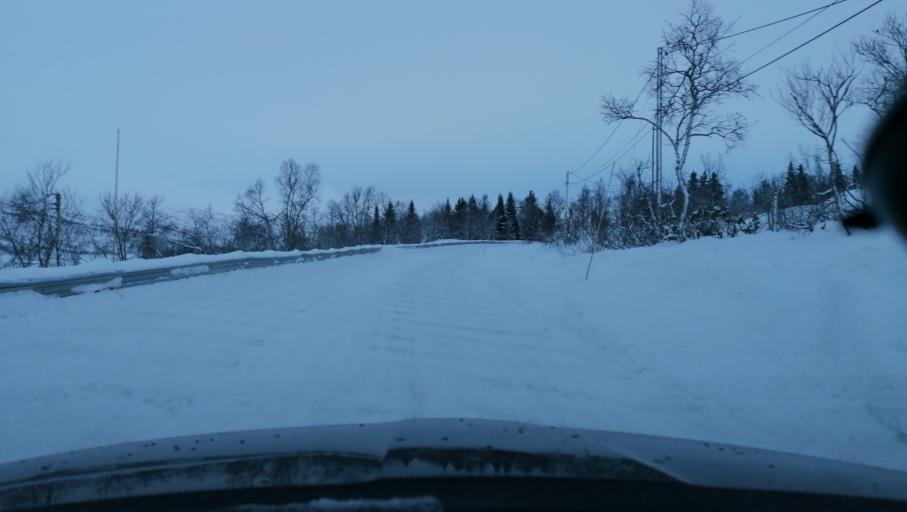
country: NO
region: Aust-Agder
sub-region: Bykle
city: Hovden
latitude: 59.6386
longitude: 7.4535
